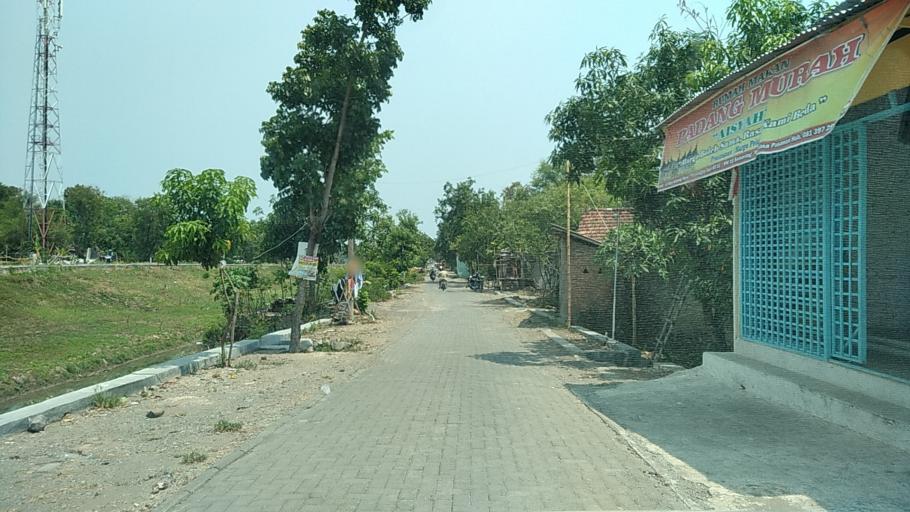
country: ID
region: Central Java
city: Mranggen
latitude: -7.0380
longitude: 110.4834
